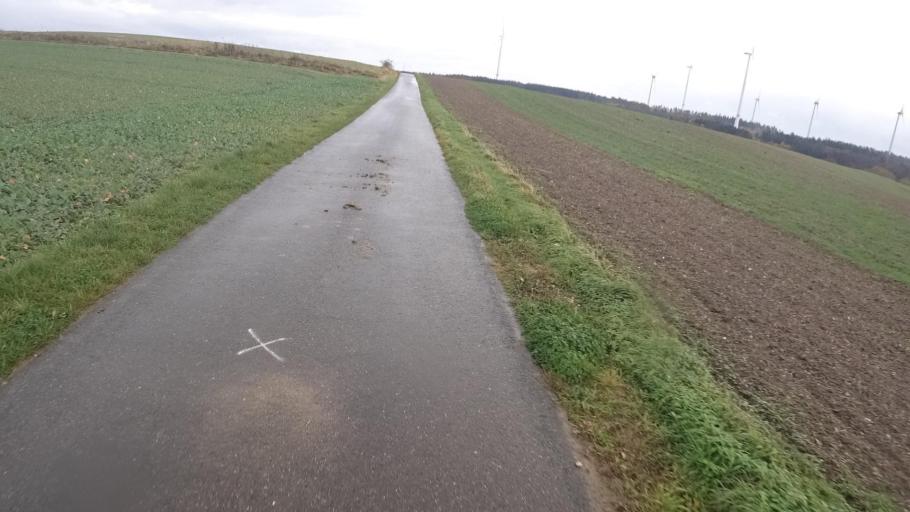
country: DE
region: Rheinland-Pfalz
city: Godenroth
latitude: 50.1121
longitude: 7.4911
